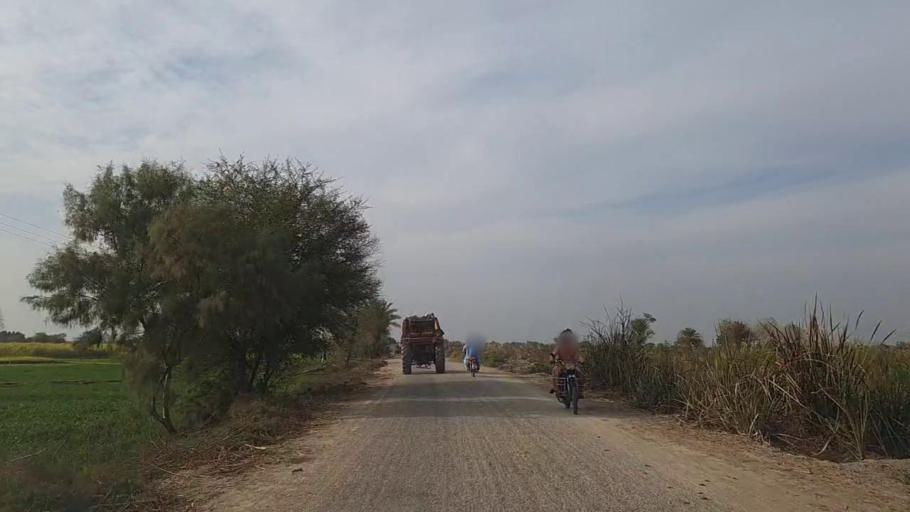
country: PK
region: Sindh
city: Daur
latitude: 26.4879
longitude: 68.4623
